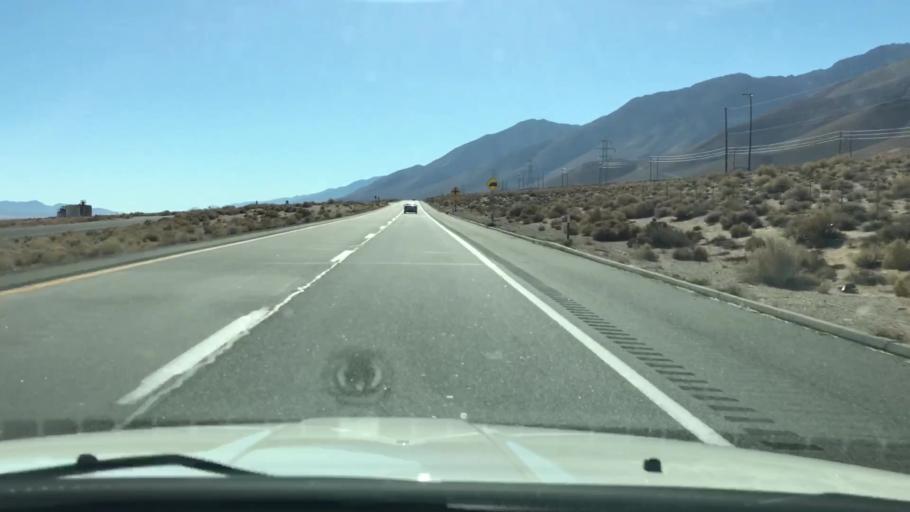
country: US
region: California
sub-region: Inyo County
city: Lone Pine
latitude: 36.4856
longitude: -118.0348
